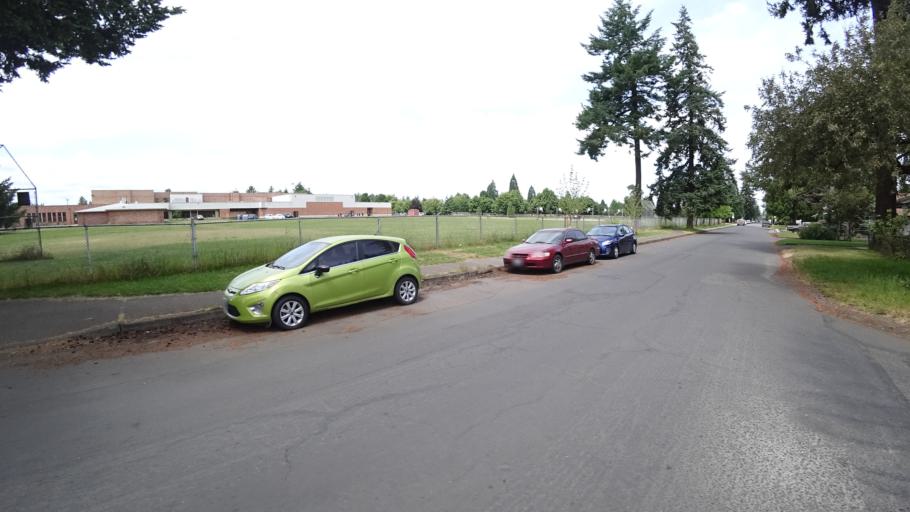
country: US
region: Oregon
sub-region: Multnomah County
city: Lents
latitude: 45.4710
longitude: -122.5996
